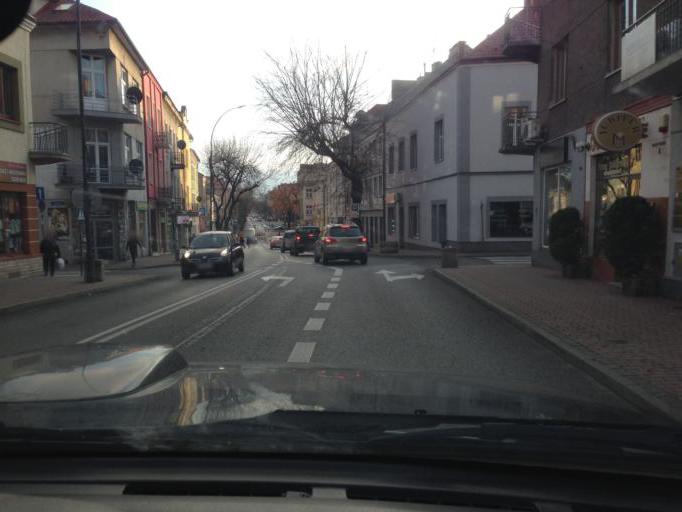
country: PL
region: Subcarpathian Voivodeship
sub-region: Powiat jasielski
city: Jaslo
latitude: 49.7467
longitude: 21.4736
